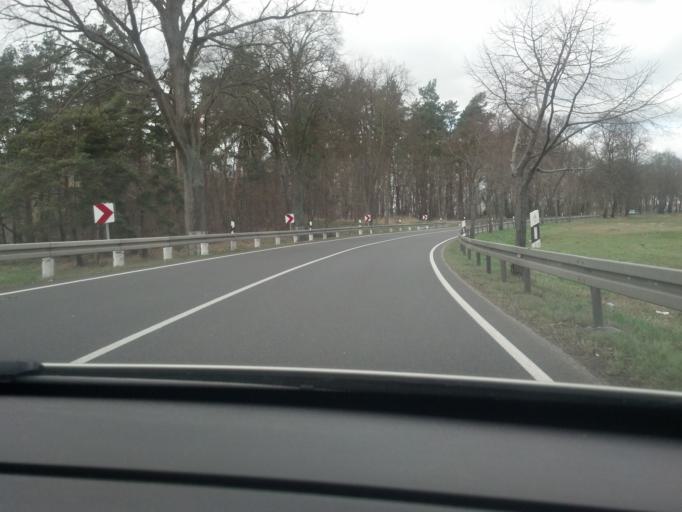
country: DE
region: Mecklenburg-Vorpommern
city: Neustrelitz
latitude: 53.3109
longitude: 13.1006
